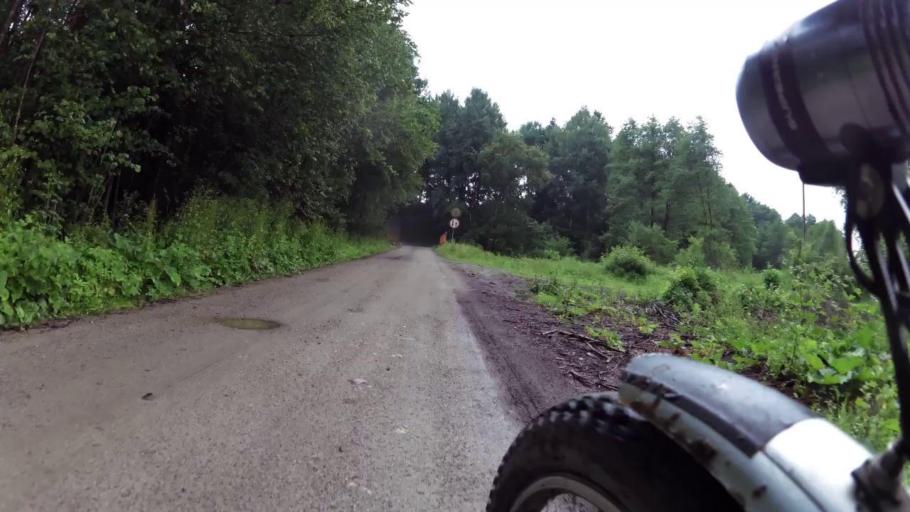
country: PL
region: West Pomeranian Voivodeship
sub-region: Powiat lobeski
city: Lobez
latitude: 53.7251
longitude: 15.6806
